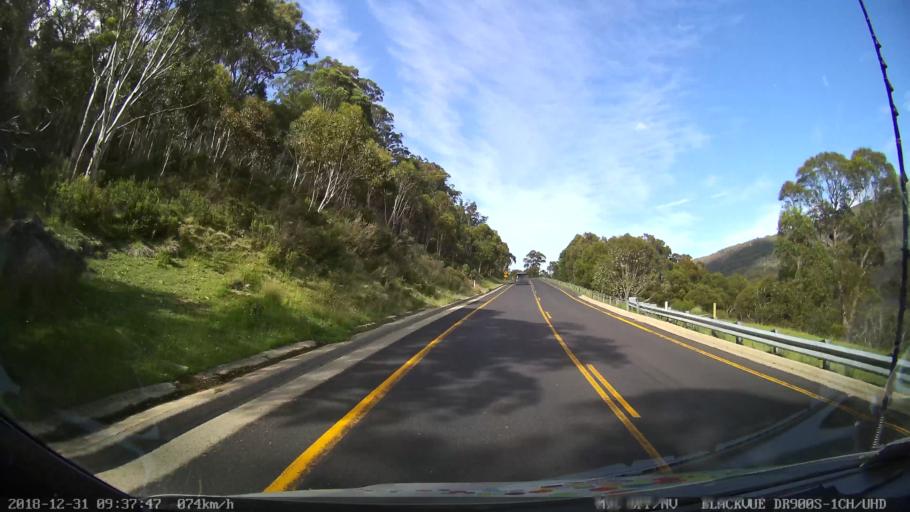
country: AU
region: New South Wales
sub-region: Snowy River
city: Jindabyne
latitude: -36.4697
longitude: 148.3735
